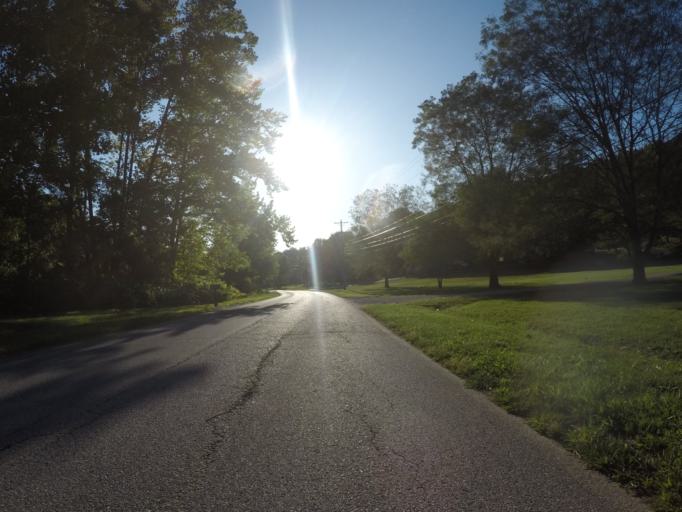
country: US
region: Ohio
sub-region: Lawrence County
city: Coal Grove
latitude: 38.5389
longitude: -82.5371
